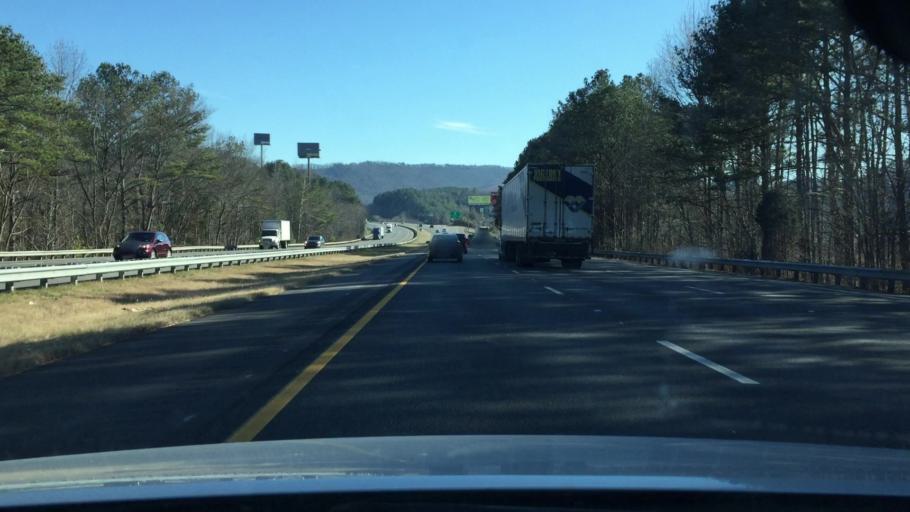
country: US
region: Georgia
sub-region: Whitfield County
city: Varnell
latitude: 34.8669
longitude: -85.0345
